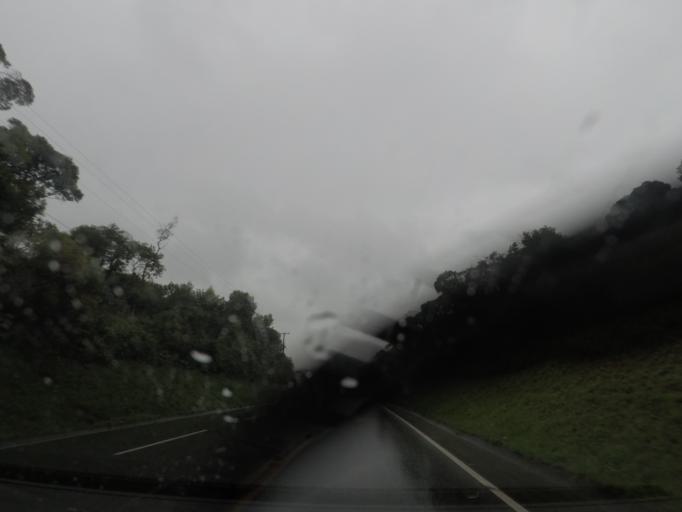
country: BR
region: Parana
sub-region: Almirante Tamandare
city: Almirante Tamandare
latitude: -25.3652
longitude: -49.3209
